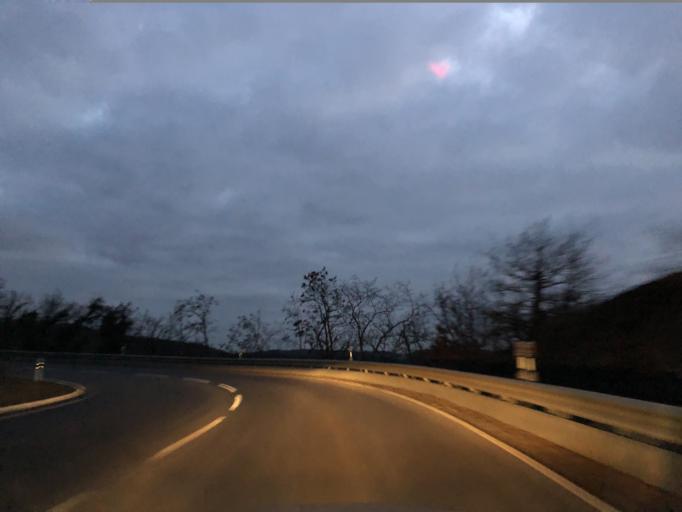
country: DE
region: Rheinland-Pfalz
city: Nassau
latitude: 50.2983
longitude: 7.8110
